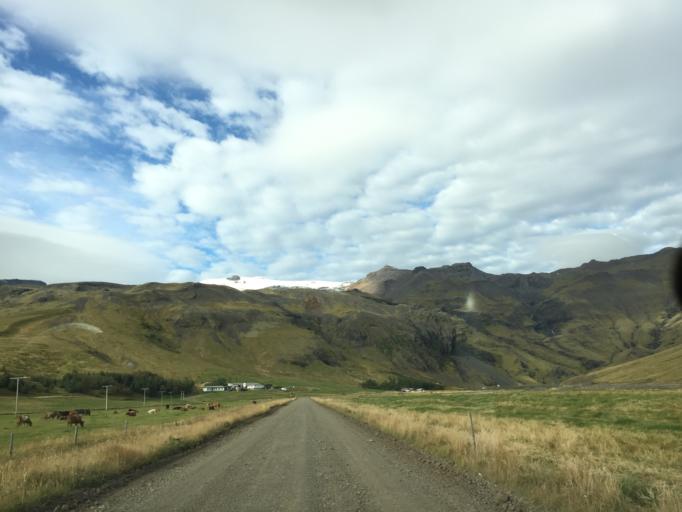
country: IS
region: South
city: Vestmannaeyjar
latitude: 63.5538
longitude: -19.6263
